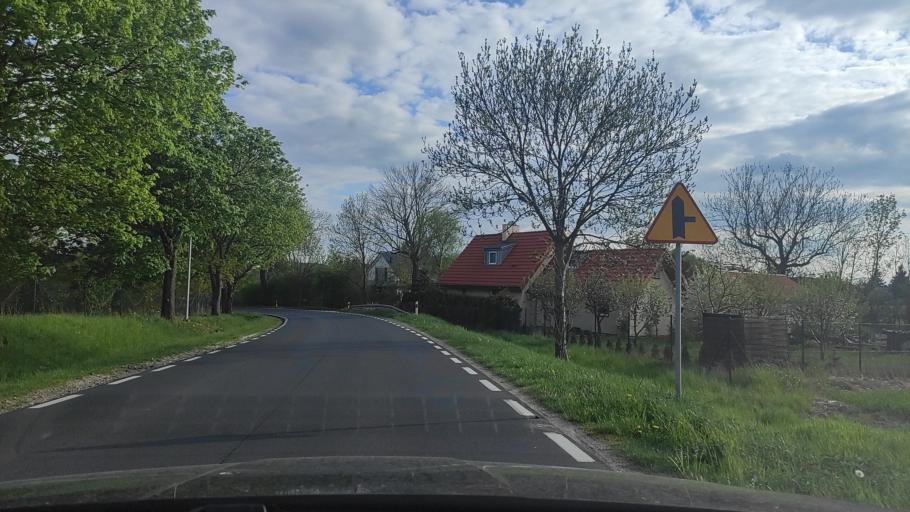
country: PL
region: Greater Poland Voivodeship
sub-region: Powiat poznanski
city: Kostrzyn
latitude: 52.4212
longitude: 17.2269
